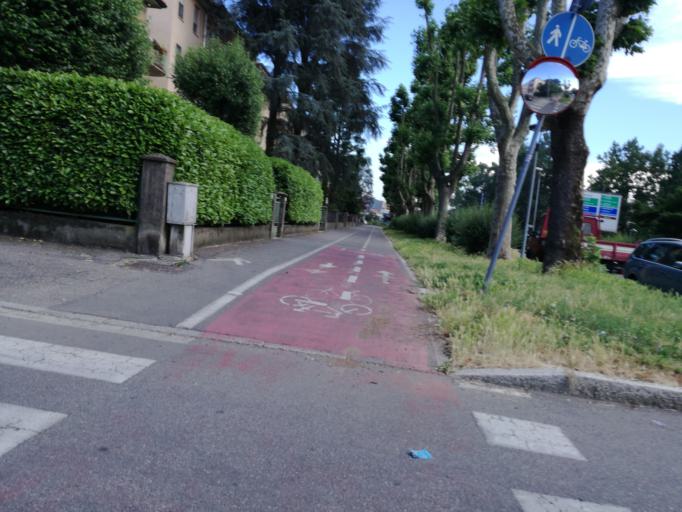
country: IT
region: Piedmont
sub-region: Provincia di Novara
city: Novara
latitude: 45.4364
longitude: 8.6196
